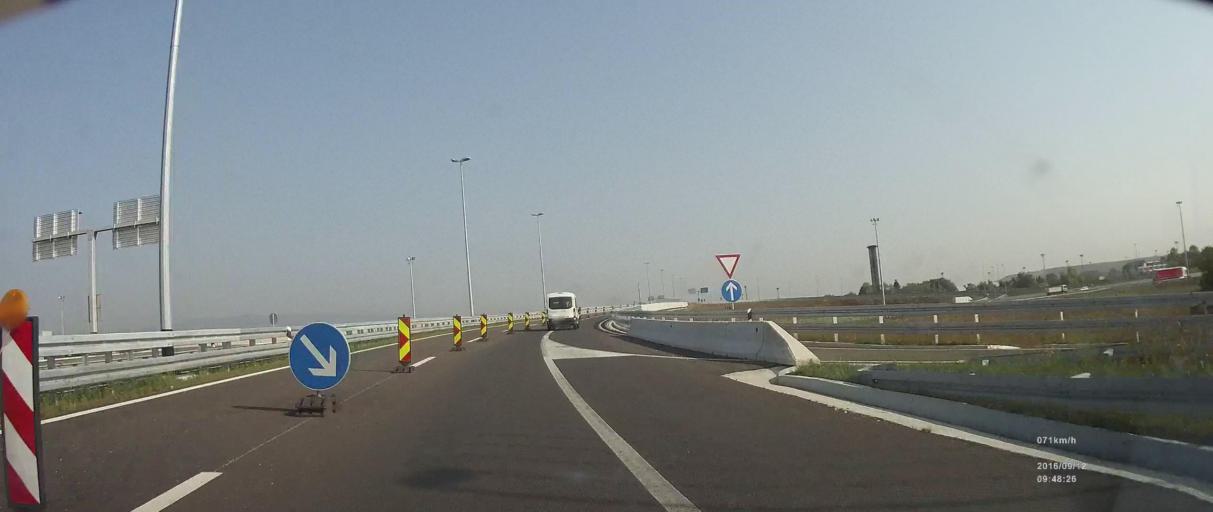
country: HR
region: Grad Zagreb
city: Odra
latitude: 45.7499
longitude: 16.0042
